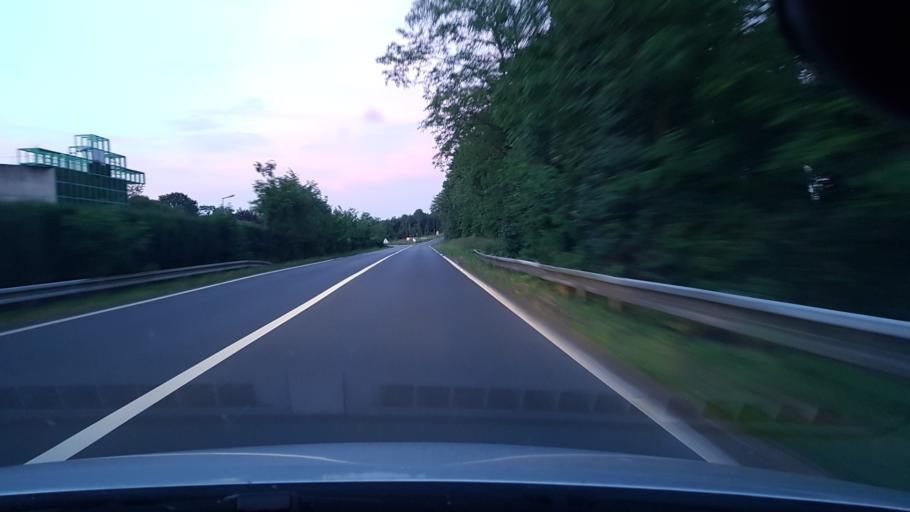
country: FR
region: Ile-de-France
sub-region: Departement de l'Essonne
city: Villebon-sur-Yvette
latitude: 48.6970
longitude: 2.2314
